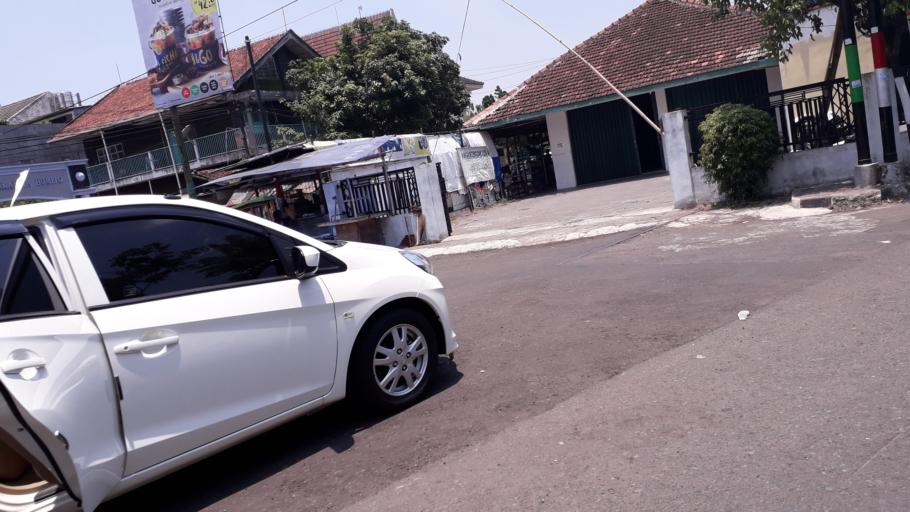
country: ID
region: Daerah Istimewa Yogyakarta
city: Yogyakarta
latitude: -7.7856
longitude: 110.3606
